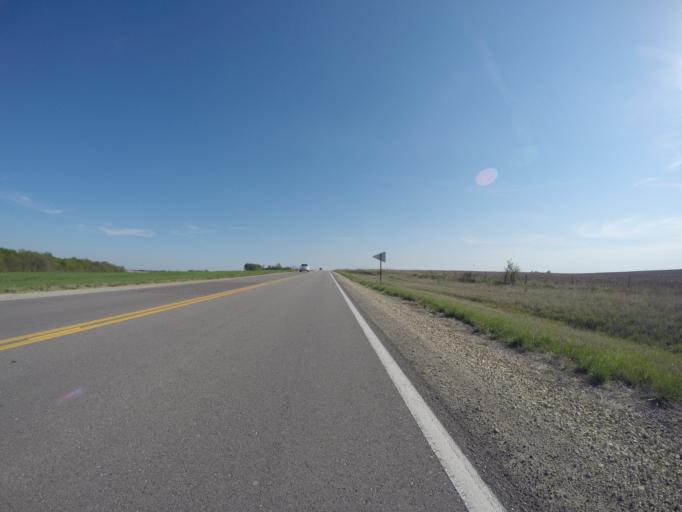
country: US
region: Kansas
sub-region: Riley County
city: Fort Riley North
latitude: 39.2956
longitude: -96.7750
